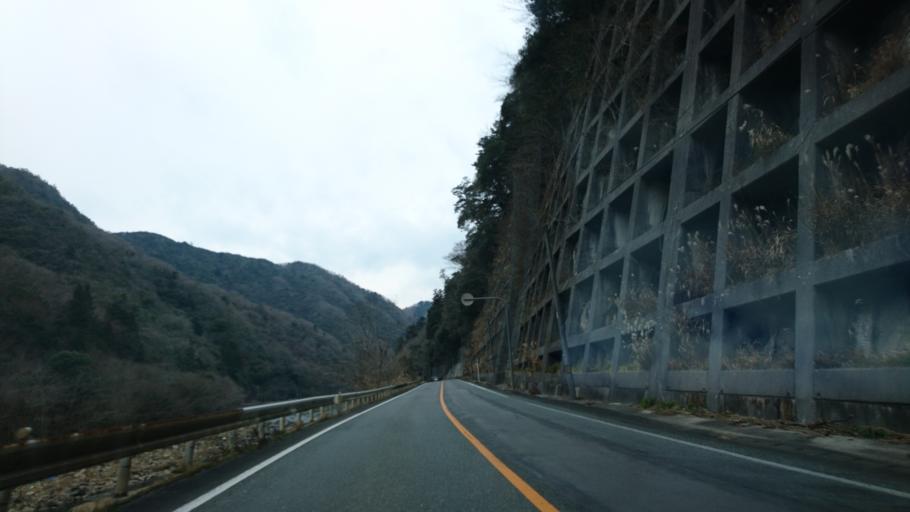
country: JP
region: Okayama
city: Niimi
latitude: 34.8965
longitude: 133.5429
